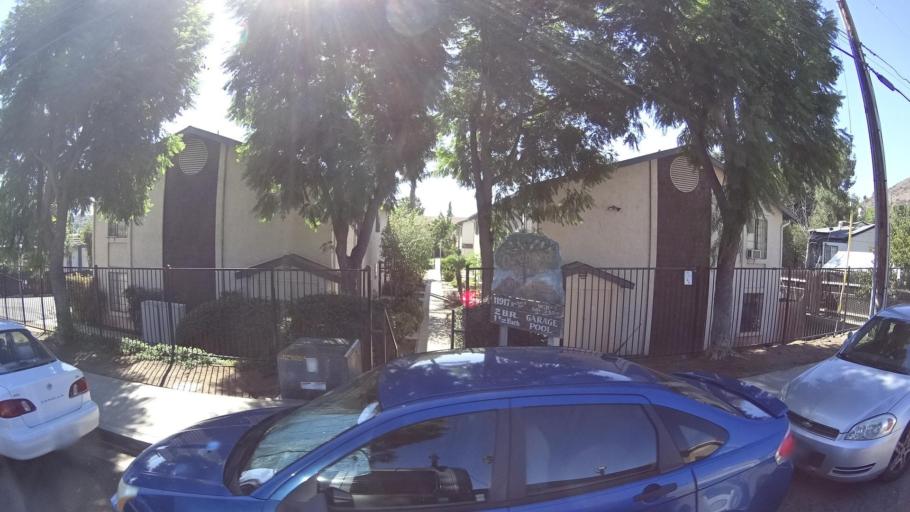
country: US
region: California
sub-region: San Diego County
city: Winter Gardens
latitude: 32.8259
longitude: -116.9343
